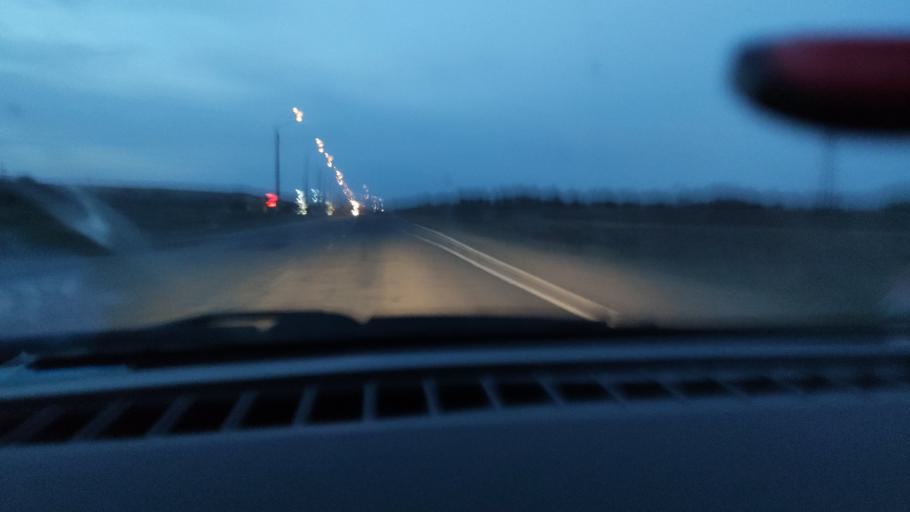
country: RU
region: Saratov
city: Sinodskoye
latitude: 52.0826
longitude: 46.7977
